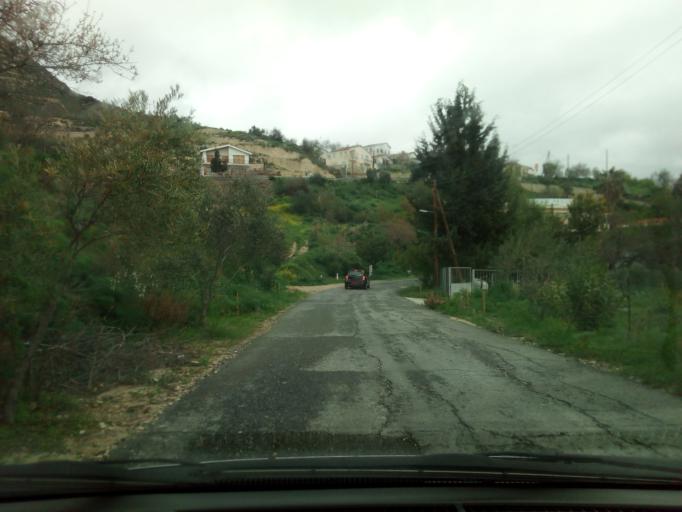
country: CY
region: Lefkosia
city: Lythrodontas
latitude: 34.8618
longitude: 33.3068
